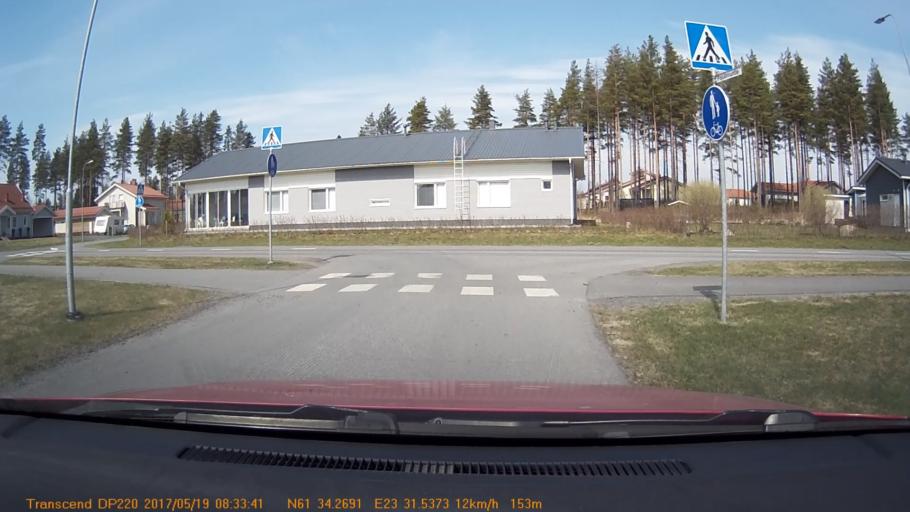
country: FI
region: Pirkanmaa
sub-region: Tampere
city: Yloejaervi
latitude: 61.5711
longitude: 23.5257
